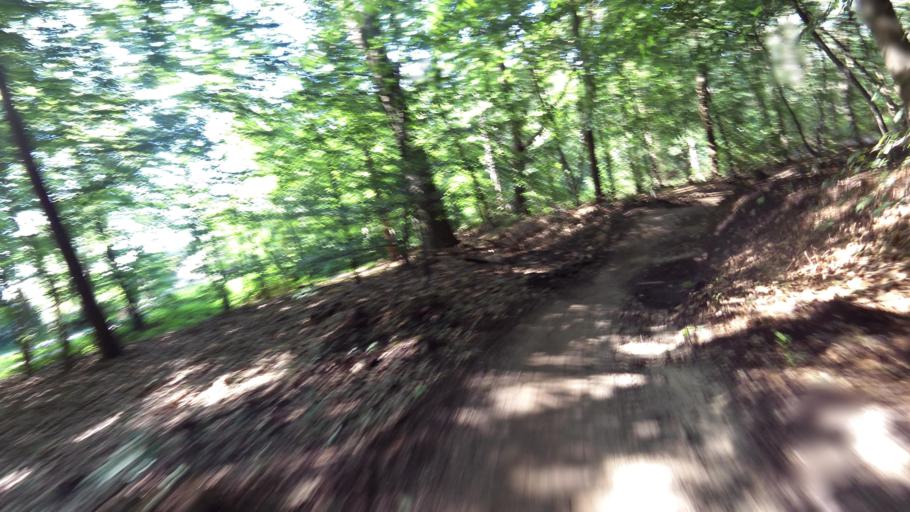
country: NL
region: Gelderland
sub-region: Gemeente Arnhem
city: Hoogkamp
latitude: 52.0077
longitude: 5.8819
